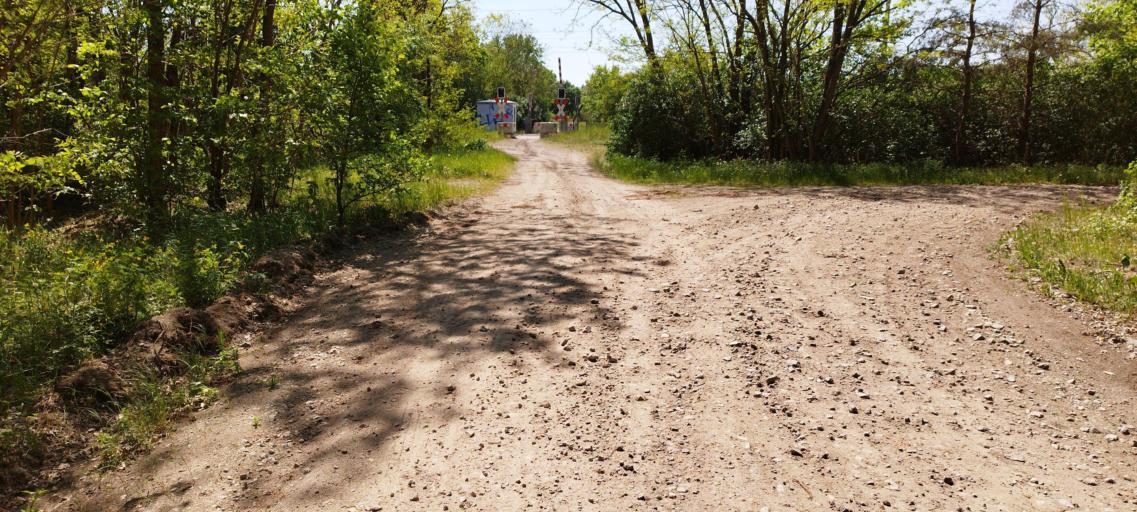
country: DE
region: Brandenburg
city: Rauen
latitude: 52.3789
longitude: 14.0121
